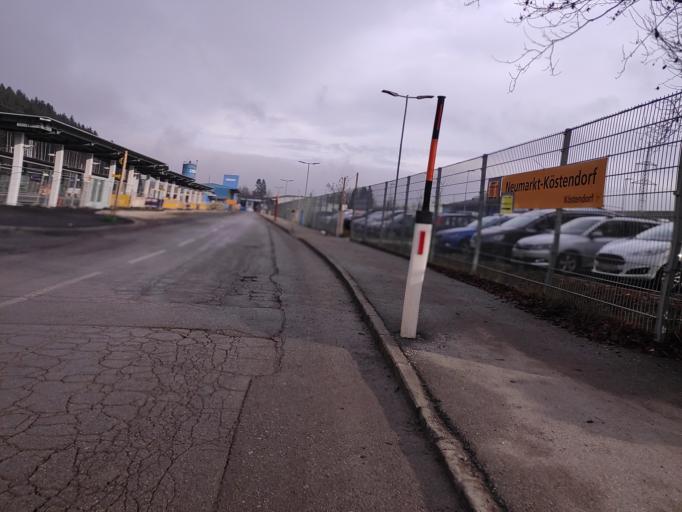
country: AT
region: Salzburg
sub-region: Politischer Bezirk Salzburg-Umgebung
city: Neumarkt am Wallersee
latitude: 47.9543
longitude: 13.2251
